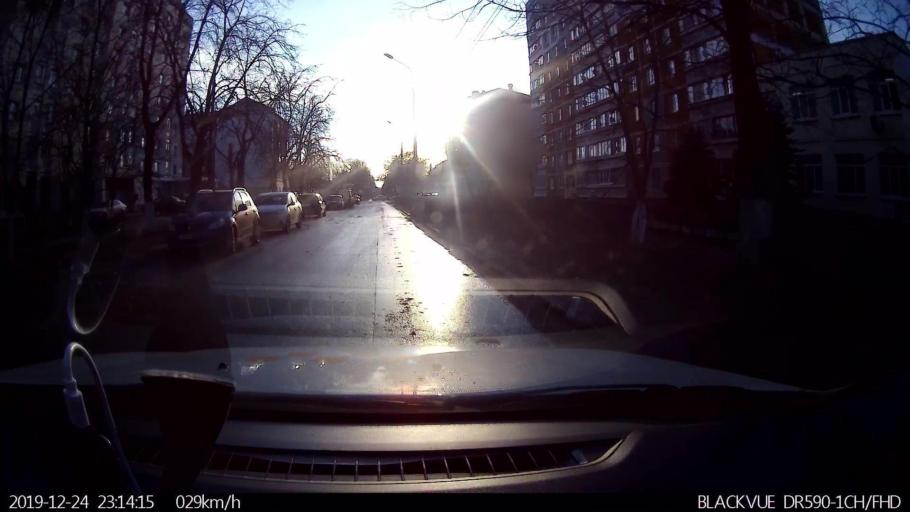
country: RU
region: Nizjnij Novgorod
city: Gorbatovka
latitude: 56.2504
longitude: 43.8582
